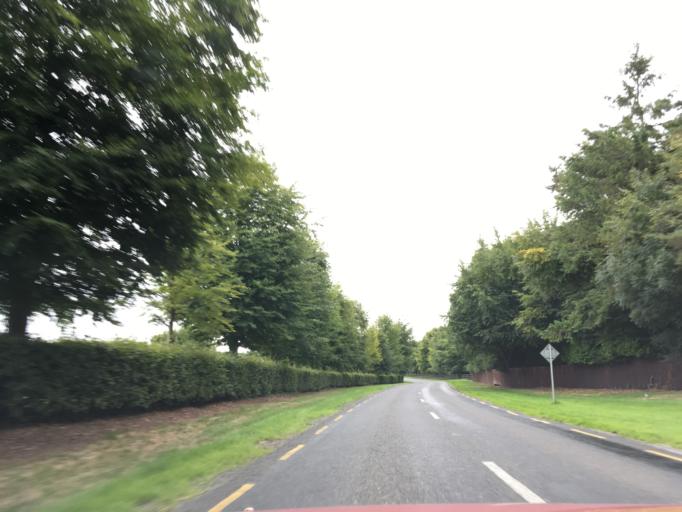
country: IE
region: Munster
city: Cashel
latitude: 52.4636
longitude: -7.8282
